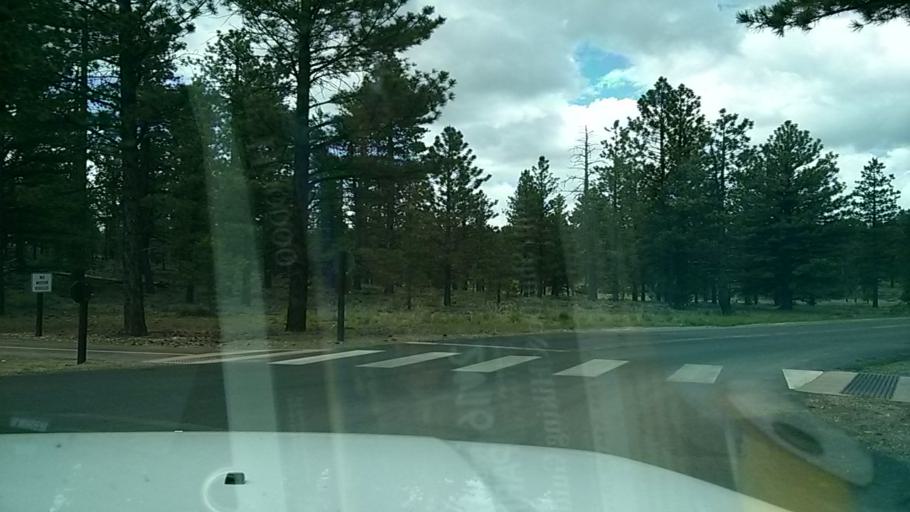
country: US
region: Utah
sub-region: Garfield County
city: Panguitch
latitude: 37.6337
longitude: -112.1661
